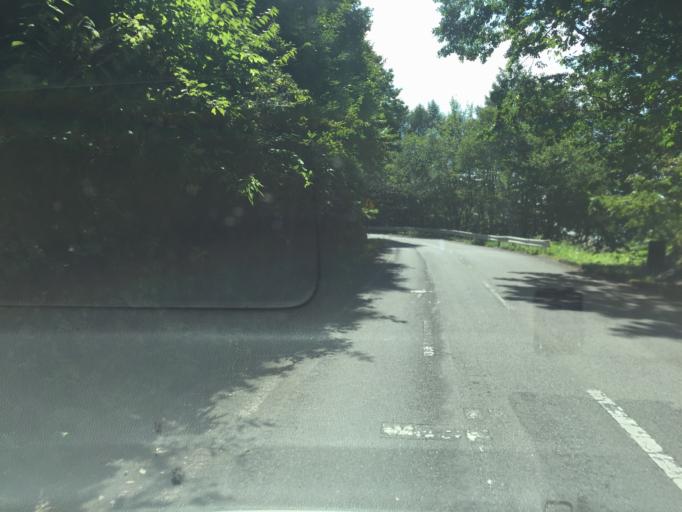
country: JP
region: Fukushima
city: Inawashiro
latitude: 37.6602
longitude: 140.1496
